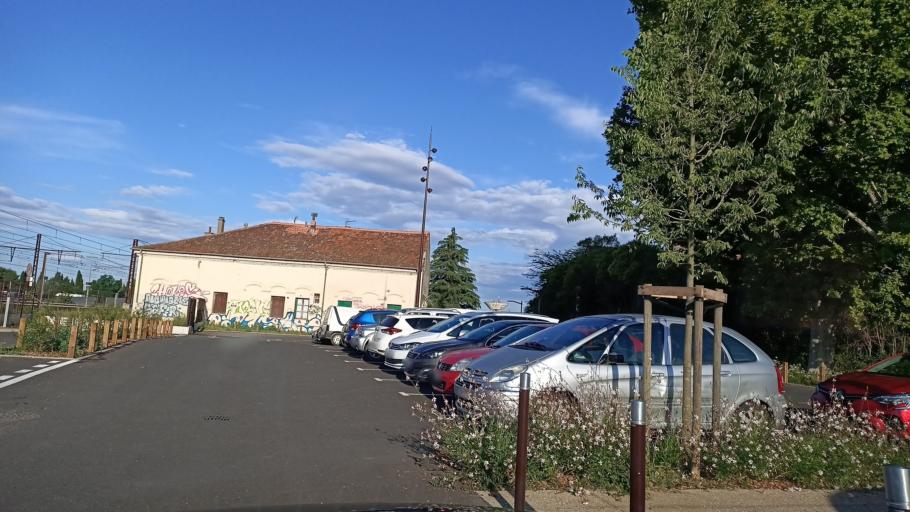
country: FR
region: Languedoc-Roussillon
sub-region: Departement de l'Herault
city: Lunel
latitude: 43.6800
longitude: 4.1312
